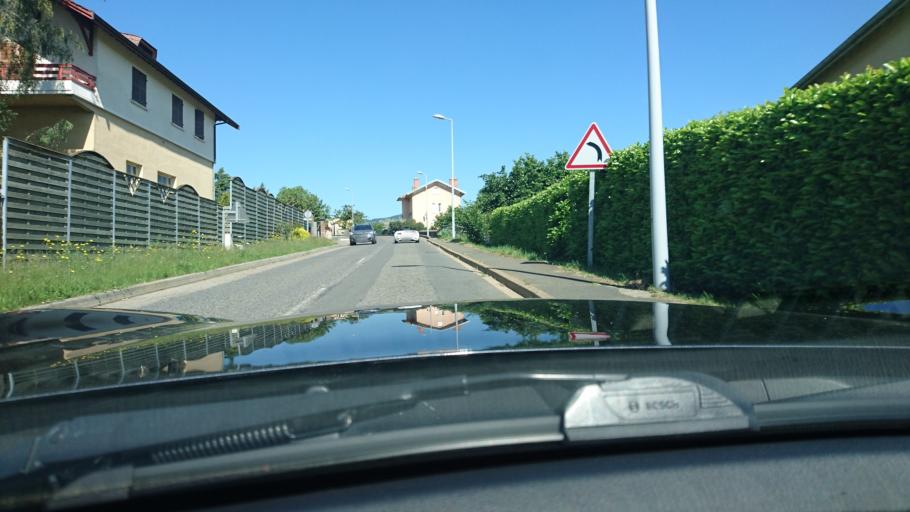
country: FR
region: Rhone-Alpes
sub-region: Departement du Rhone
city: Bessenay
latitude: 45.7779
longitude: 4.5567
